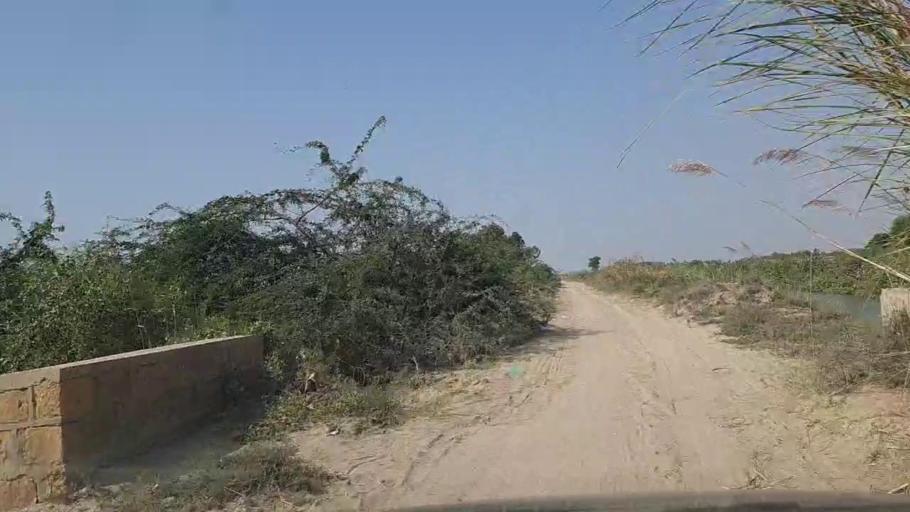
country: PK
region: Sindh
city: Gharo
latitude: 24.7279
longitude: 67.7042
